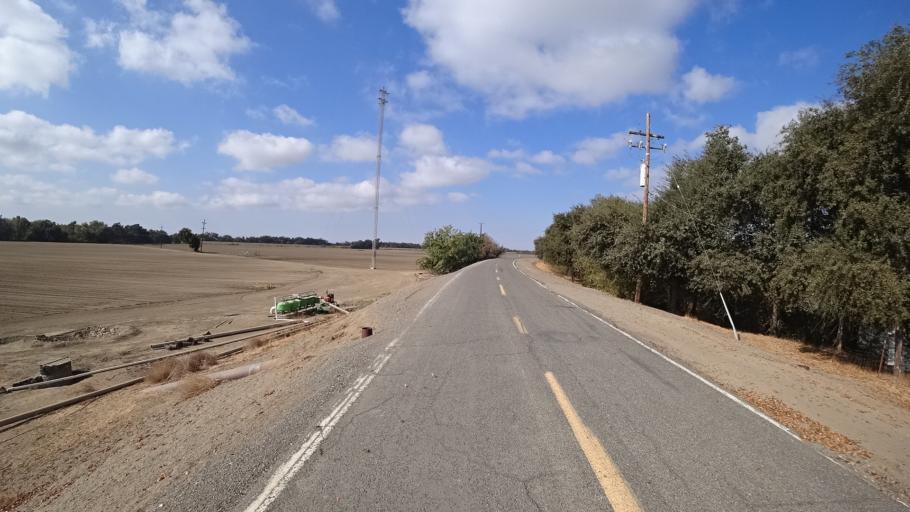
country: US
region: California
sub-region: Yolo County
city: Woodland
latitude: 38.7630
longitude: -121.6872
